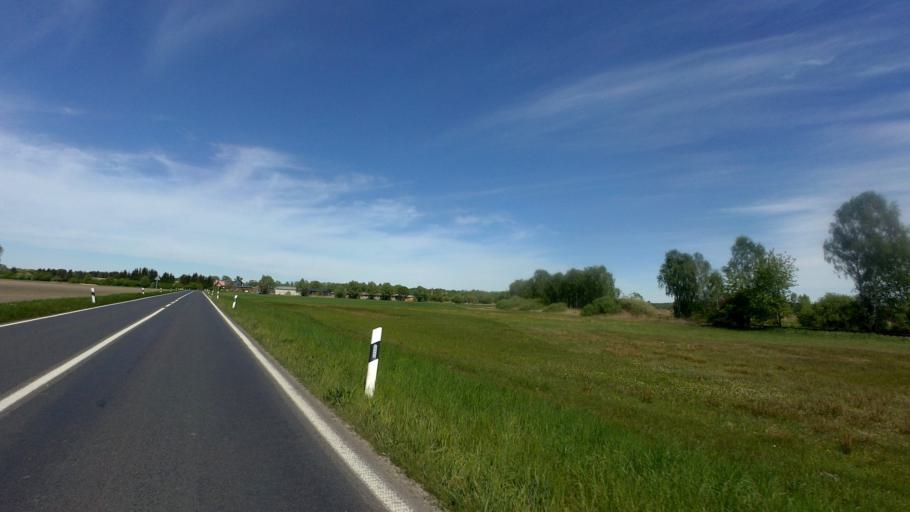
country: DE
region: Brandenburg
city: Sperenberg
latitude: 52.1288
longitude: 13.3672
